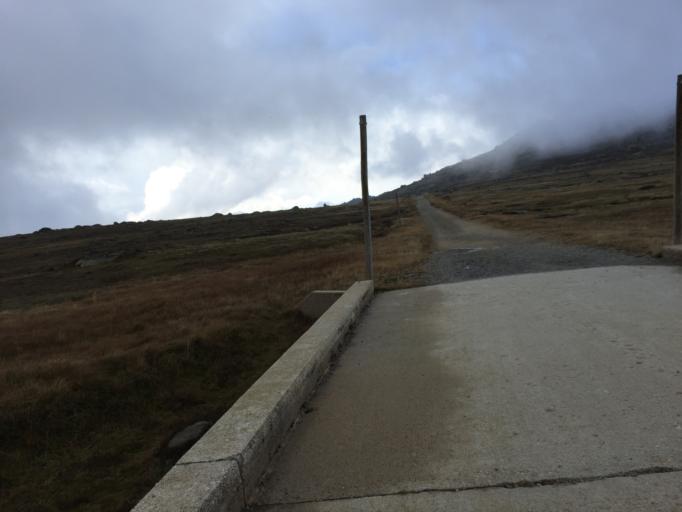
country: AU
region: New South Wales
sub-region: Snowy River
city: Jindabyne
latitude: -36.4585
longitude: 148.2968
